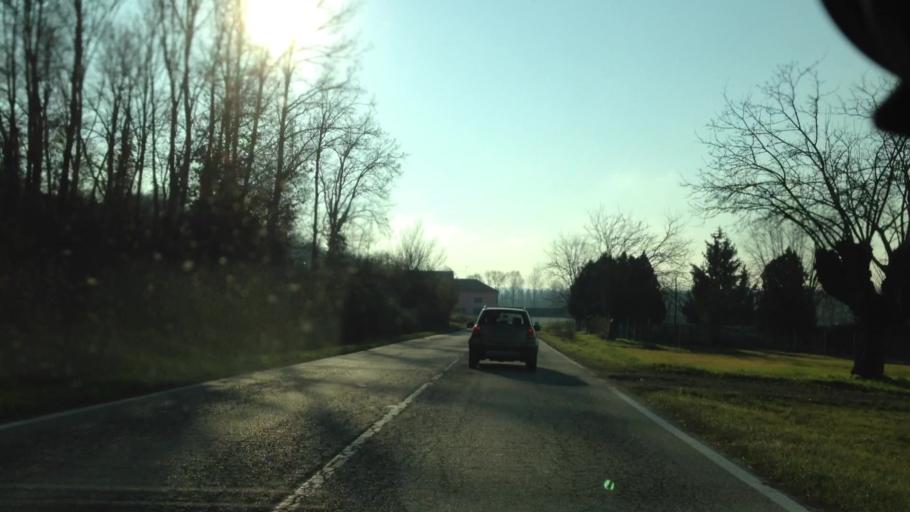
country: IT
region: Piedmont
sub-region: Provincia di Alessandria
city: Masio
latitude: 44.8677
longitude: 8.4264
